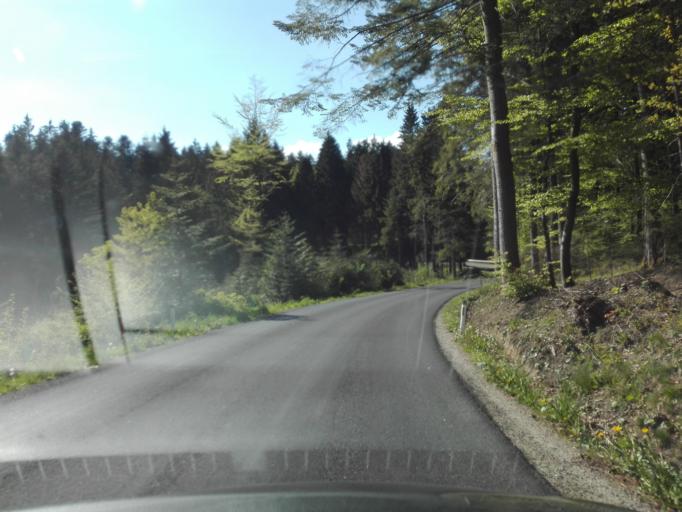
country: DE
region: Bavaria
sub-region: Lower Bavaria
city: Obernzell
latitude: 48.4458
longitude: 13.6789
